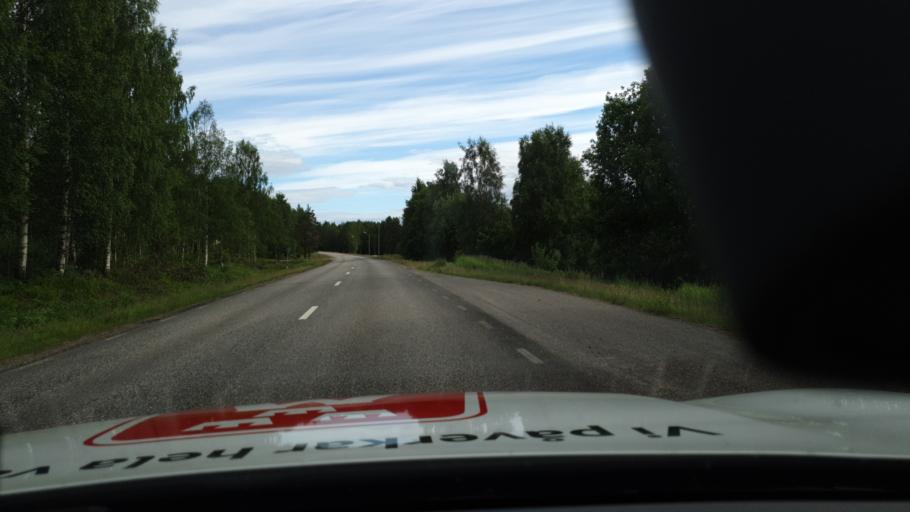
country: SE
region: Norrbotten
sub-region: Overkalix Kommun
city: OEverkalix
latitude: 66.5402
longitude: 22.7538
